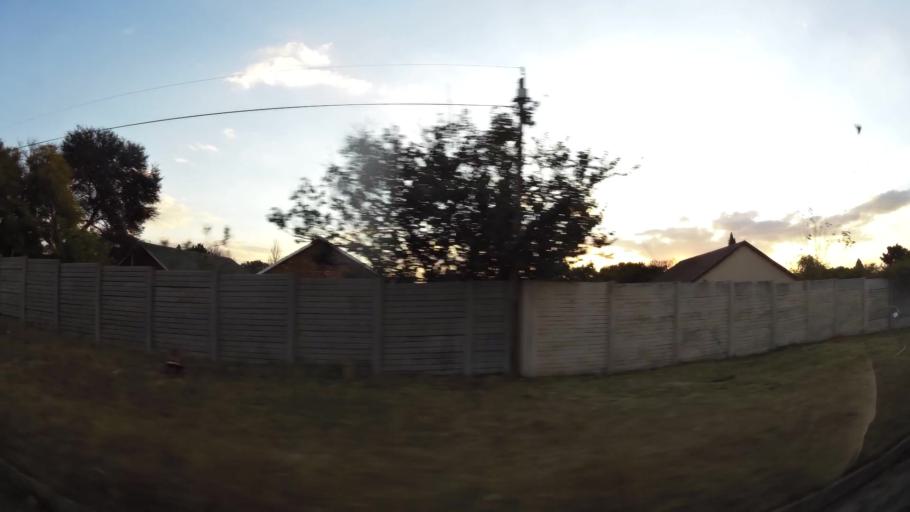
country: ZA
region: Gauteng
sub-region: West Rand District Municipality
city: Krugersdorp
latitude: -26.0751
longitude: 27.7835
